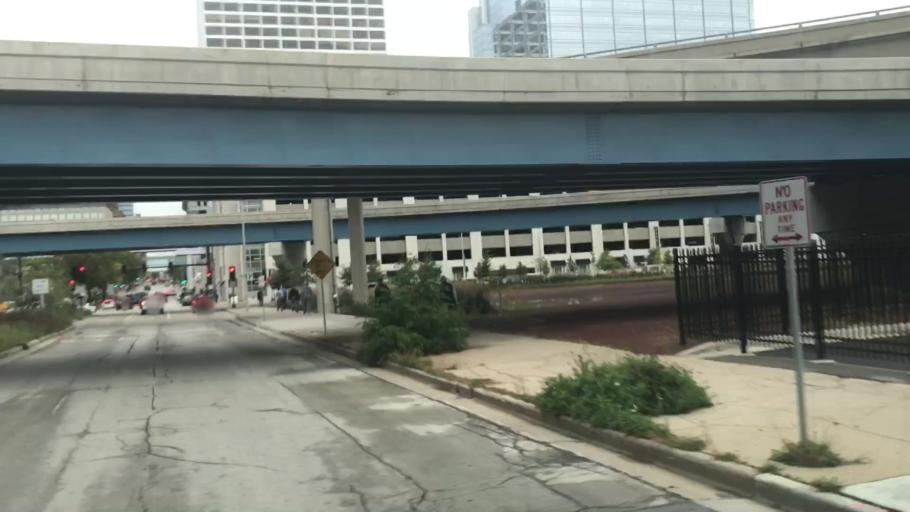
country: US
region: Wisconsin
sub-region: Milwaukee County
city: Milwaukee
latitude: 43.0354
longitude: -87.9024
